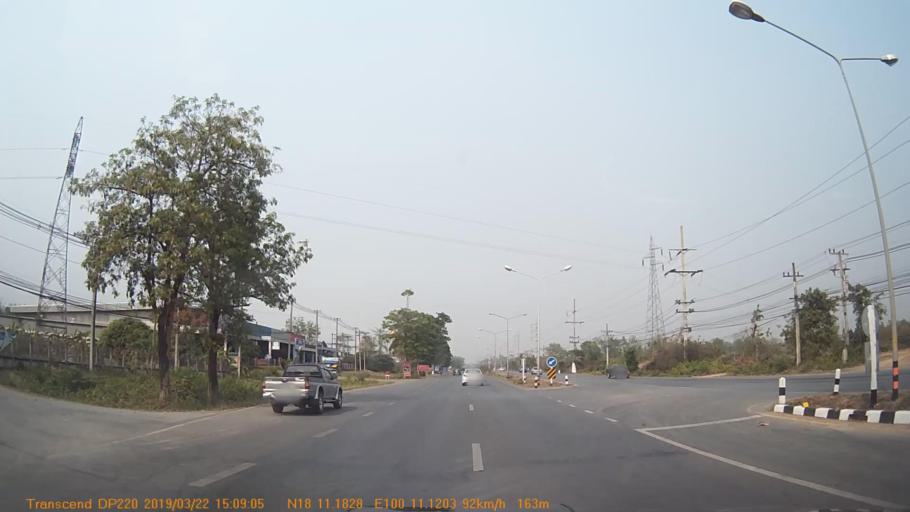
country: TH
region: Phrae
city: Phrae
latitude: 18.1866
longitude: 100.1855
